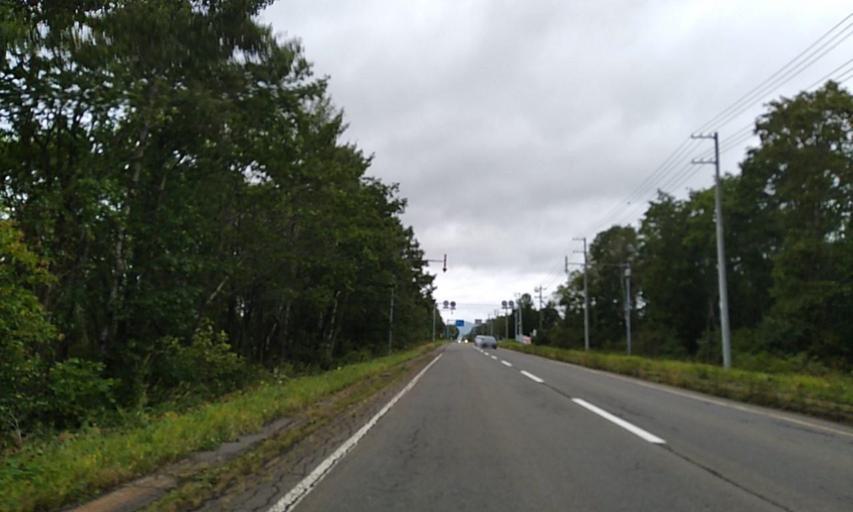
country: JP
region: Hokkaido
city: Bihoro
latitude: 43.5087
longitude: 144.4474
